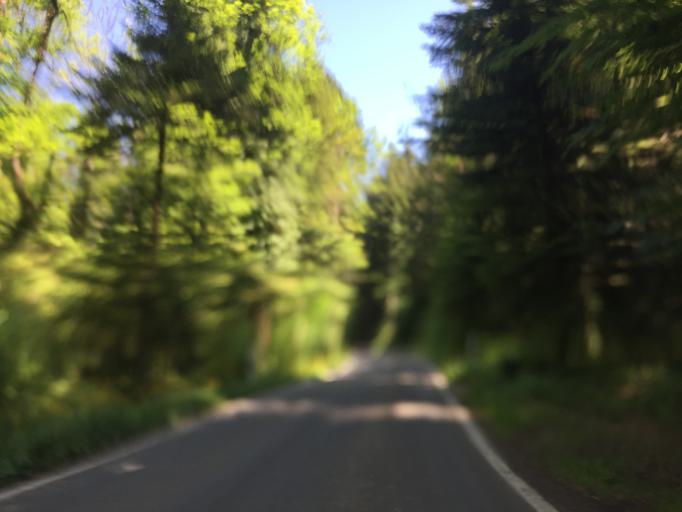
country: CH
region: Bern
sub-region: Bern-Mittelland District
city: Taegertschi
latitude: 46.8673
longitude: 7.6032
